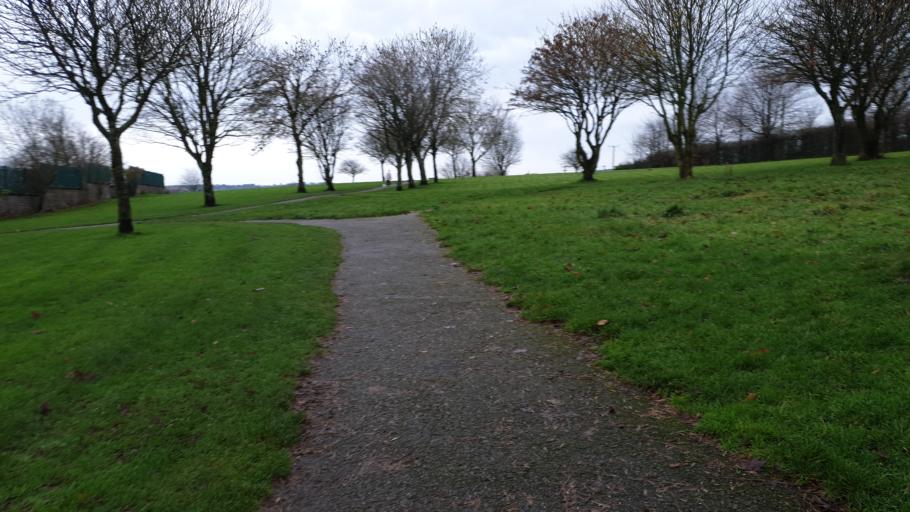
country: IE
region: Munster
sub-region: County Cork
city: Cork
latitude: 51.8902
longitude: -8.4297
